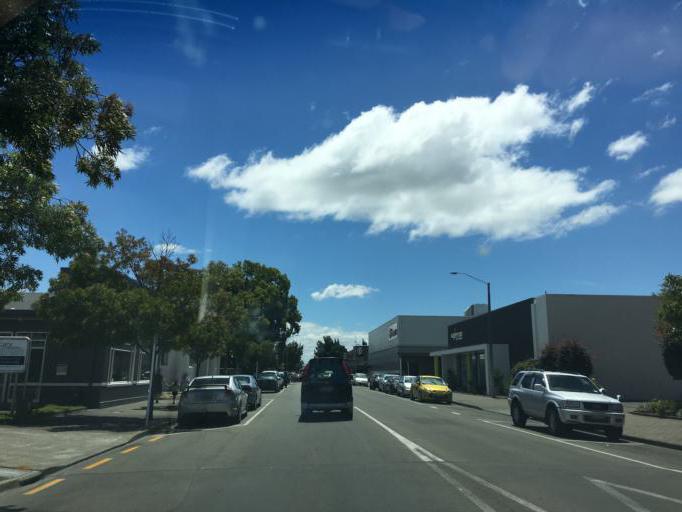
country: NZ
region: Hawke's Bay
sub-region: Hastings District
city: Hastings
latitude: -39.6417
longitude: 176.8412
